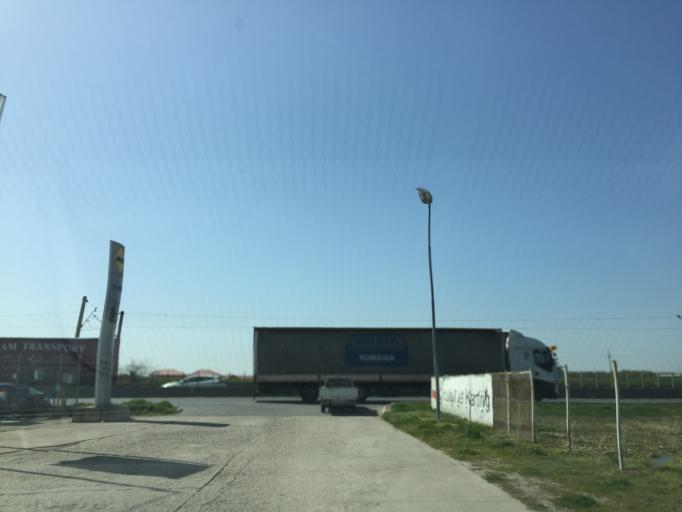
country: RO
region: Ilfov
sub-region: Comuna Tunari
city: Tunari
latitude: 44.5339
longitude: 26.1489
